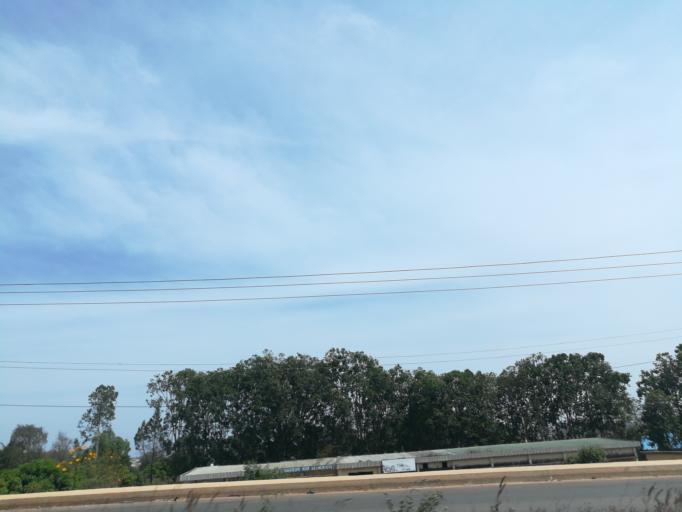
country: NG
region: Plateau
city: Bukuru
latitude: 9.8283
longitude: 8.8667
